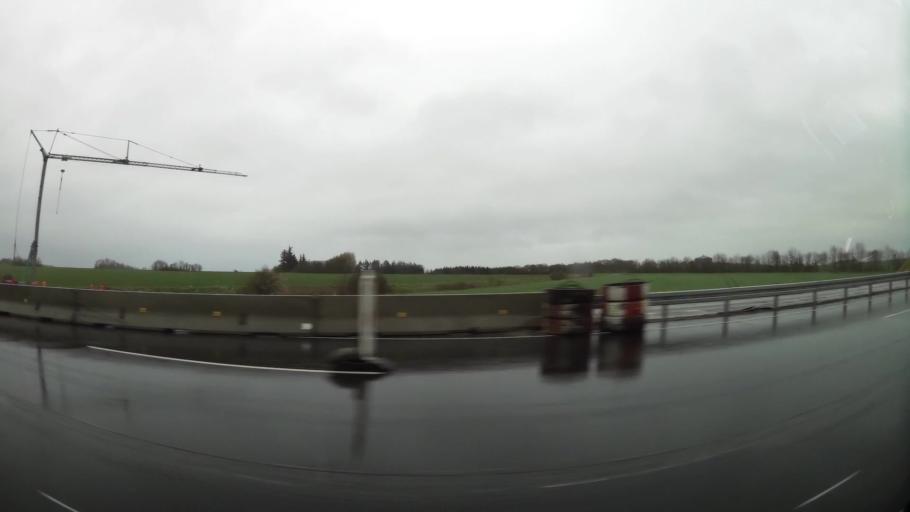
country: DK
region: Central Jutland
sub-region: Herning Kommune
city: Snejbjerg
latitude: 56.2076
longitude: 8.8684
